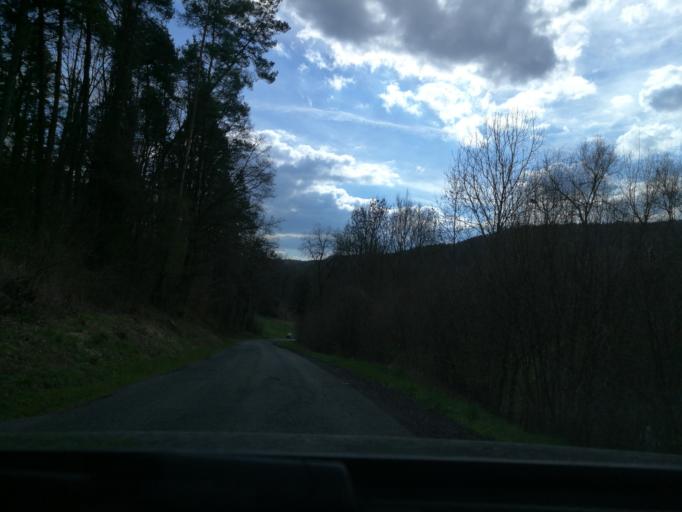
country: DE
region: Bavaria
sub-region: Upper Franconia
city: Heiligenstadt
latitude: 49.8309
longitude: 11.1218
